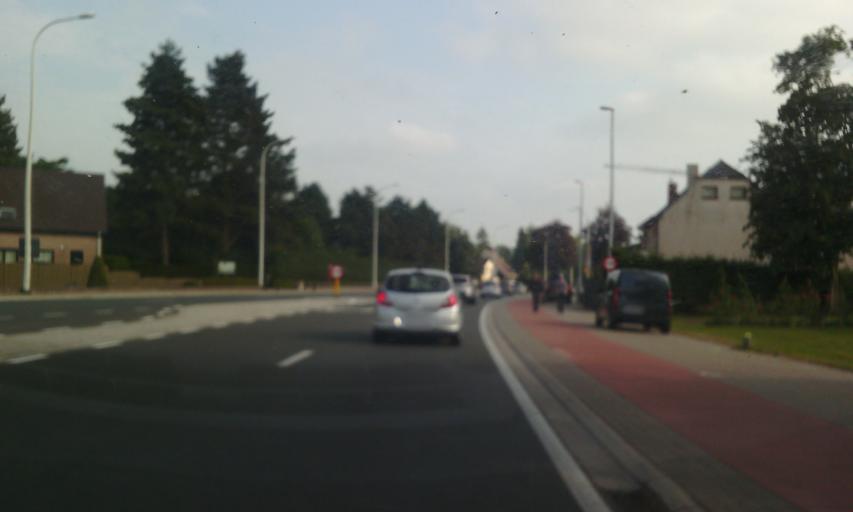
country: BE
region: Flanders
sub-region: Provincie Oost-Vlaanderen
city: Waarschoot
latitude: 51.1538
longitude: 3.5990
